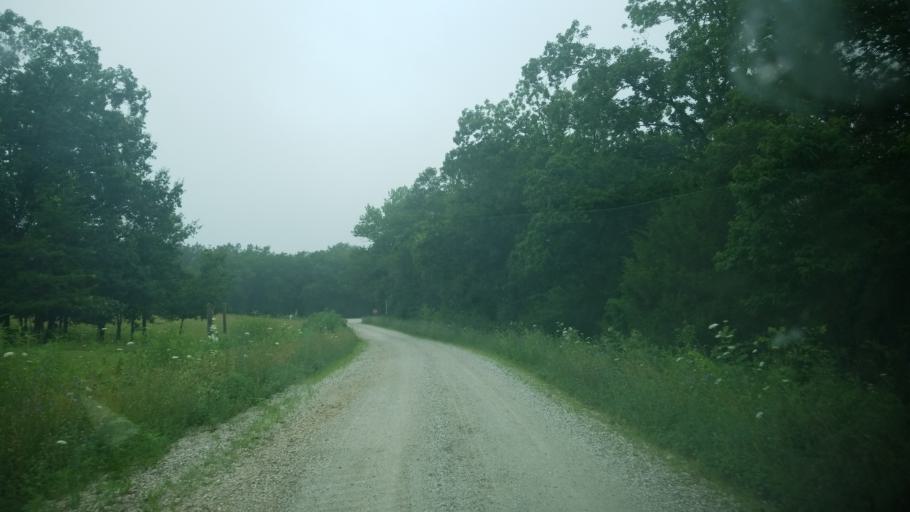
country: US
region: Missouri
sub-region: Audrain County
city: Vandalia
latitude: 39.2727
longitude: -91.3448
